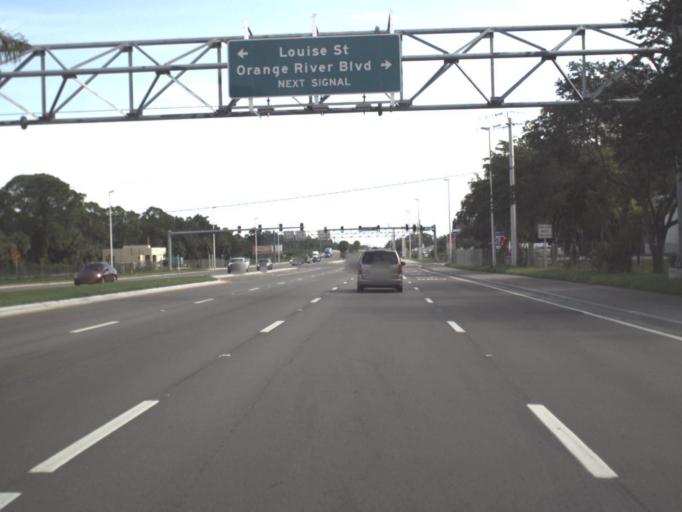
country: US
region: Florida
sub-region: Lee County
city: Tice
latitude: 26.6849
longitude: -81.7971
